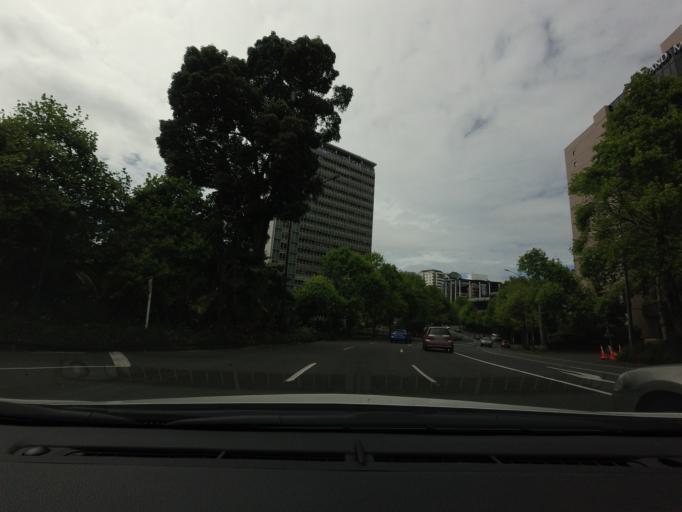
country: NZ
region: Auckland
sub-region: Auckland
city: Auckland
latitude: -36.8523
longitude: 174.7612
